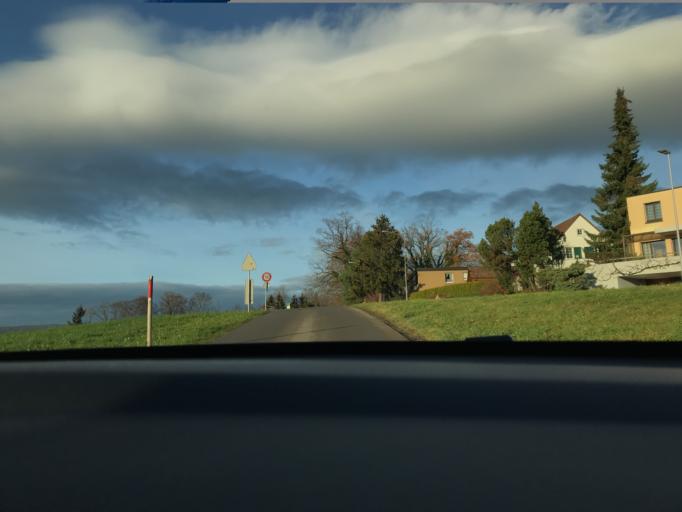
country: CH
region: Zurich
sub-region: Bezirk Dielsdorf
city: Hofstetten
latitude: 47.4716
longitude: 8.4970
